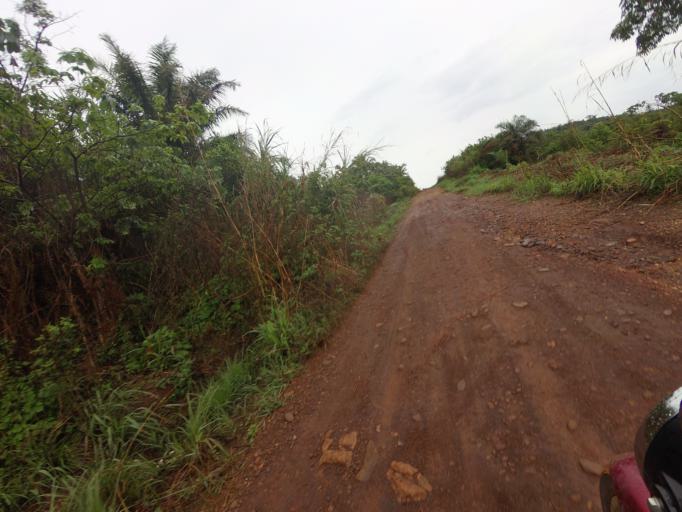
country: LR
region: Nimba
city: New Yekepa
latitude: 7.5672
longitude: -8.5544
